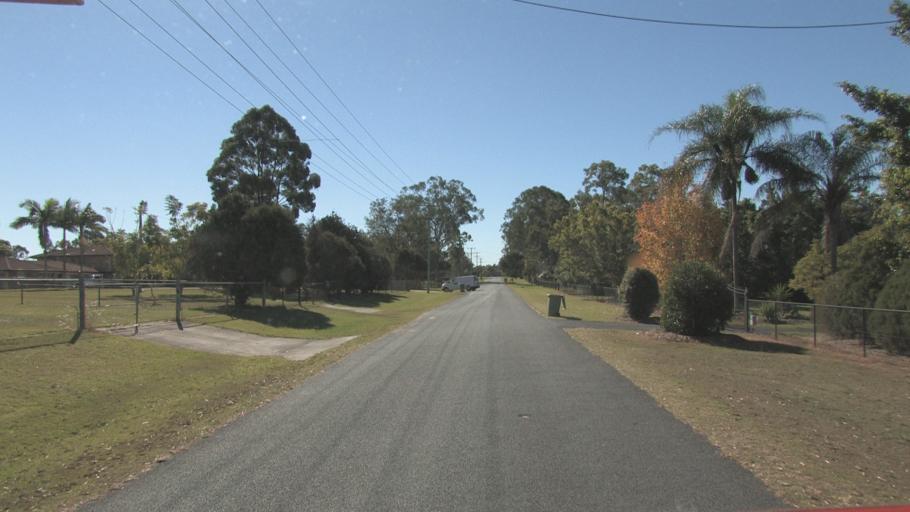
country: AU
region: Queensland
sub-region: Logan
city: Park Ridge South
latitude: -27.7261
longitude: 153.0393
